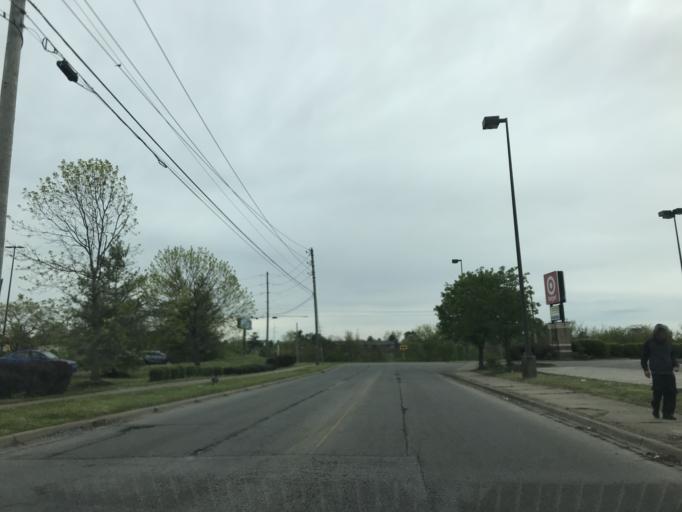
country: US
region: Kentucky
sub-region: Jefferson County
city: West Buechel
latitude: 38.1983
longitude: -85.6689
